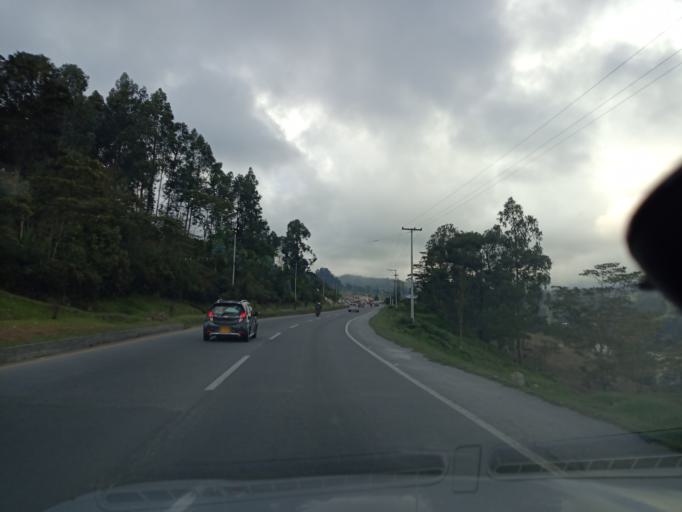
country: CO
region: Cundinamarca
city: San Antonio del Tequendama
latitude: 4.5108
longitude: -74.3619
